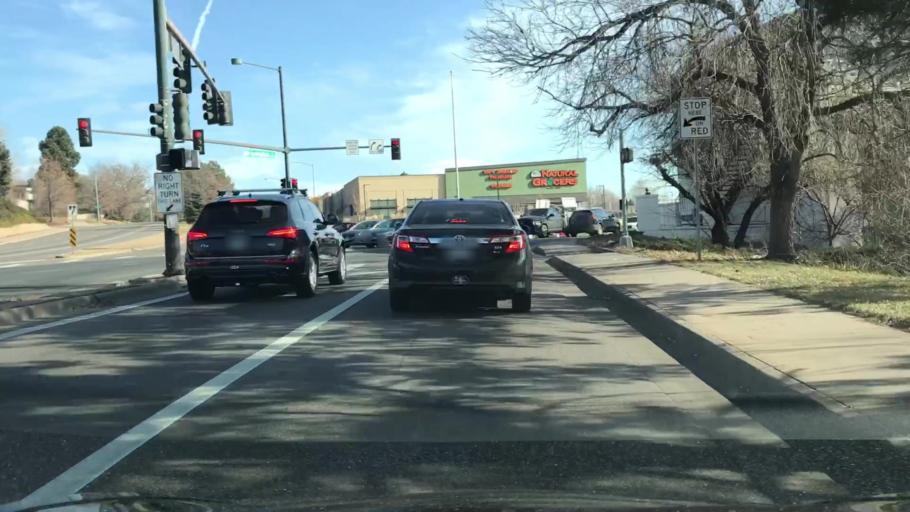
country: US
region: Colorado
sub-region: Arapahoe County
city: Glendale
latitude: 39.7112
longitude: -104.9368
